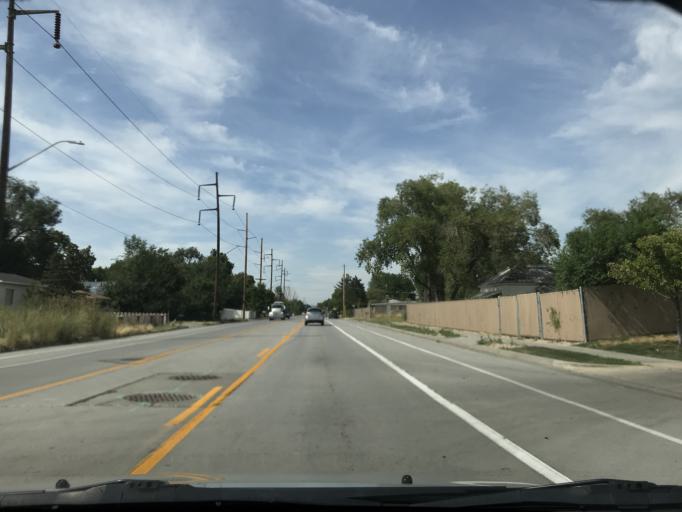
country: US
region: Utah
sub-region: Salt Lake County
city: South Salt Lake
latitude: 40.7356
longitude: -111.9168
